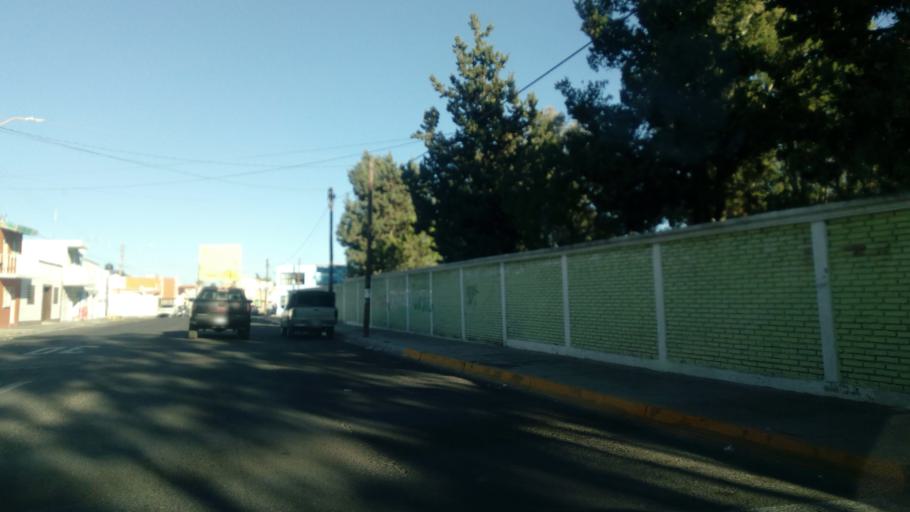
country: MX
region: Durango
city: Victoria de Durango
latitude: 24.0116
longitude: -104.6737
